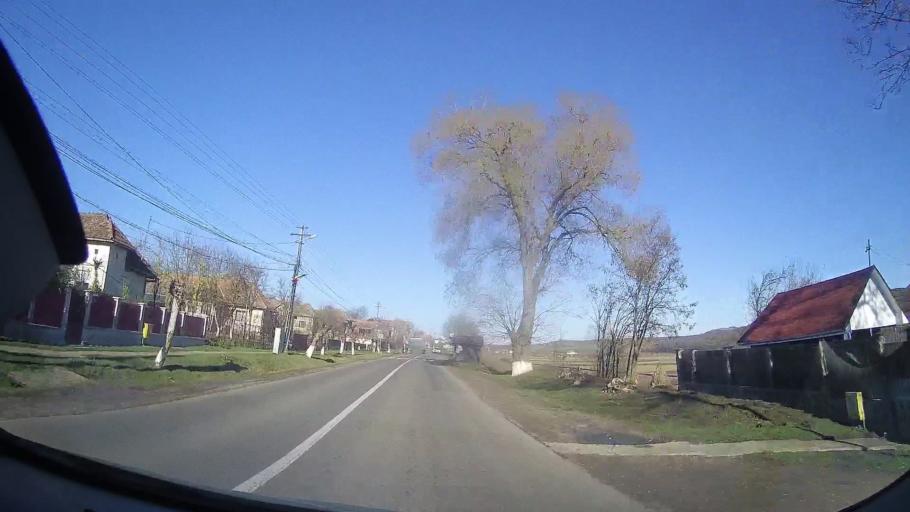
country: RO
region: Mures
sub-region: Comuna Sarmasu
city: Balda
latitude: 46.7242
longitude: 24.1432
